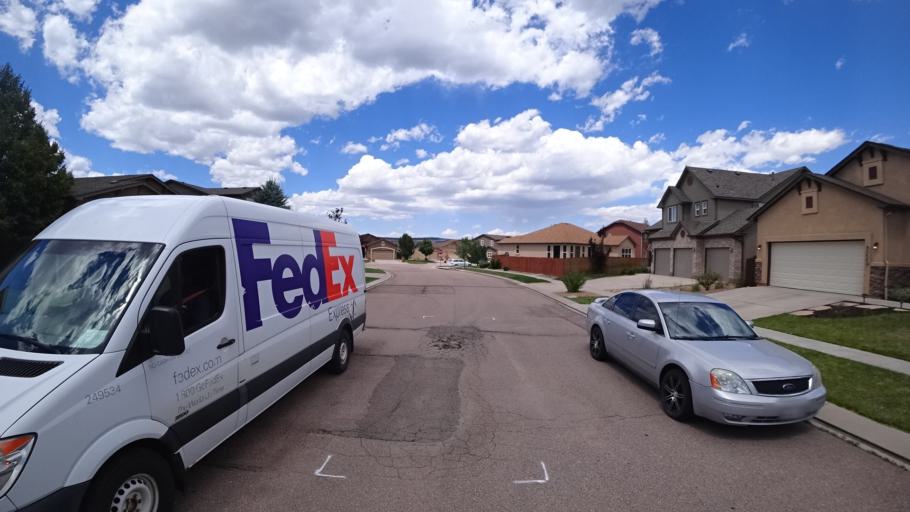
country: US
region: Colorado
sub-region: El Paso County
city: Black Forest
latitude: 38.9489
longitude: -104.7130
